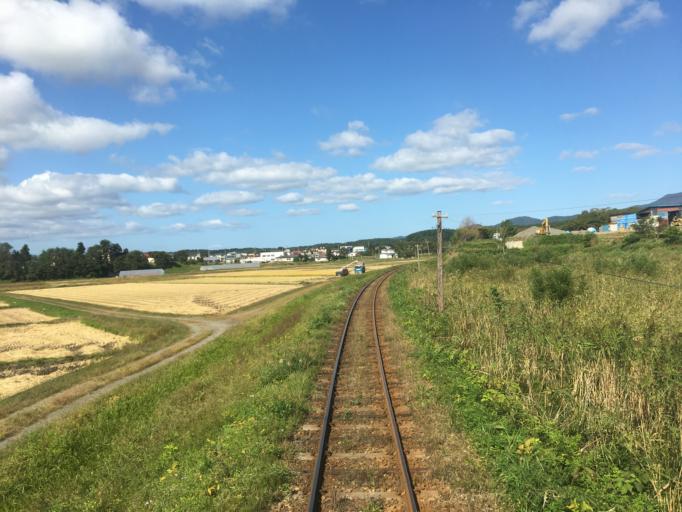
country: JP
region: Aomori
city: Goshogawara
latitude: 40.9480
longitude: 140.4381
